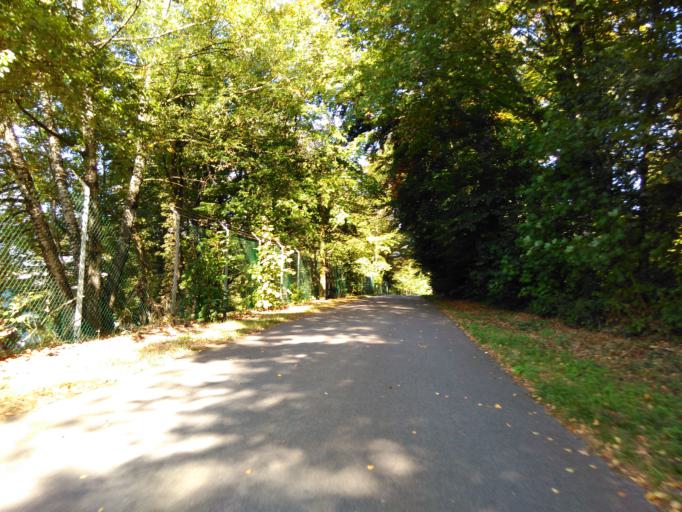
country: LU
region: Luxembourg
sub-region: Canton de Capellen
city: Steinfort
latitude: 49.6663
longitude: 5.9147
